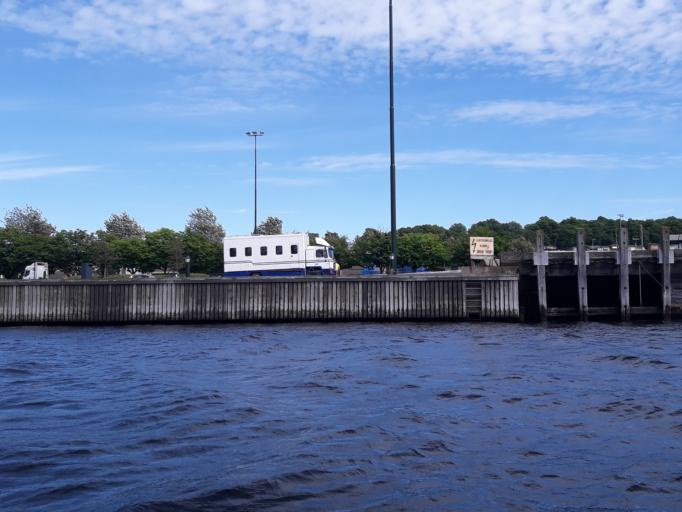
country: NO
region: Ostfold
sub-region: Moss
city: Moss
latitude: 59.4305
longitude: 10.6532
